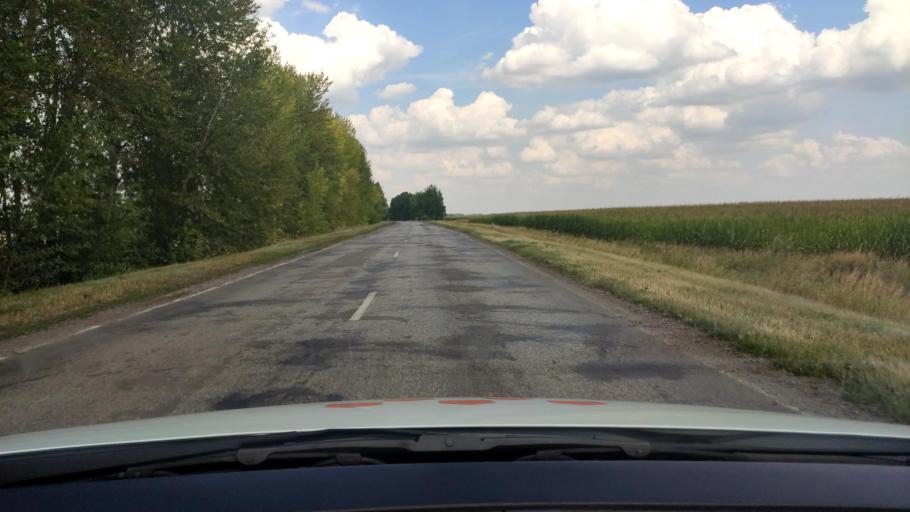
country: RU
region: Voronezj
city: Pereleshinskiy
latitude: 51.7254
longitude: 40.3689
